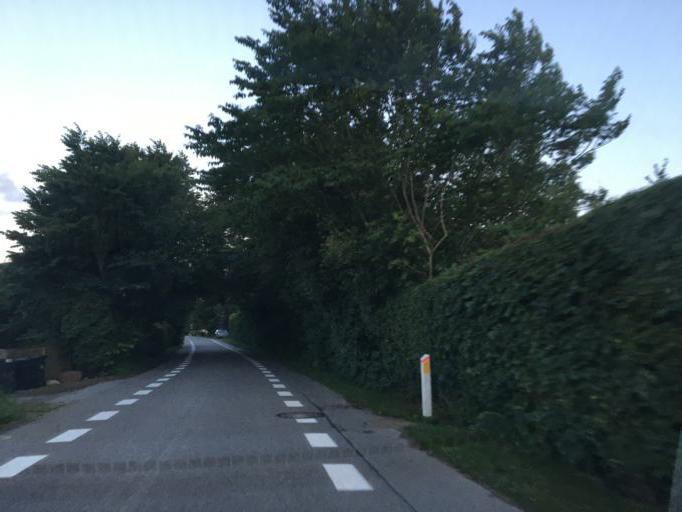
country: DK
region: Zealand
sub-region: Solrod Kommune
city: Havdrup
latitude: 55.5165
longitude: 12.1439
